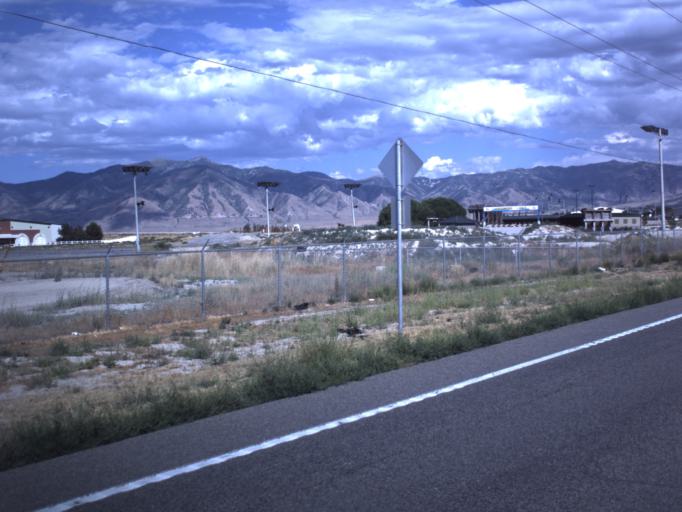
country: US
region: Utah
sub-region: Tooele County
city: Grantsville
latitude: 40.5732
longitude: -112.3818
